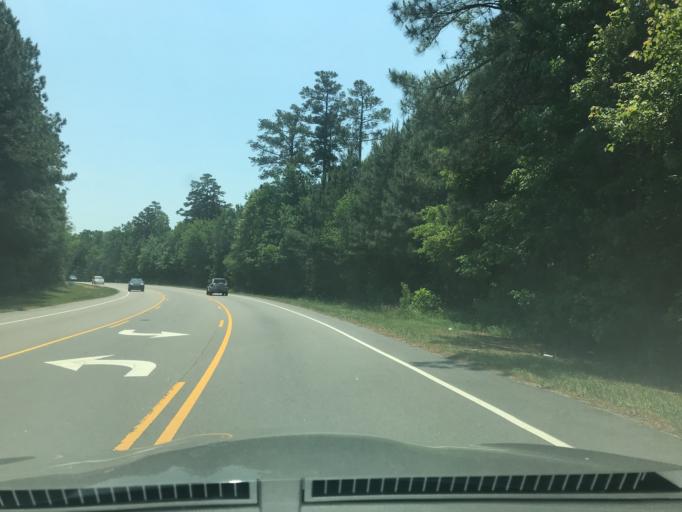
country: US
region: North Carolina
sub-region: Wake County
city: West Raleigh
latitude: 35.8901
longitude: -78.6026
